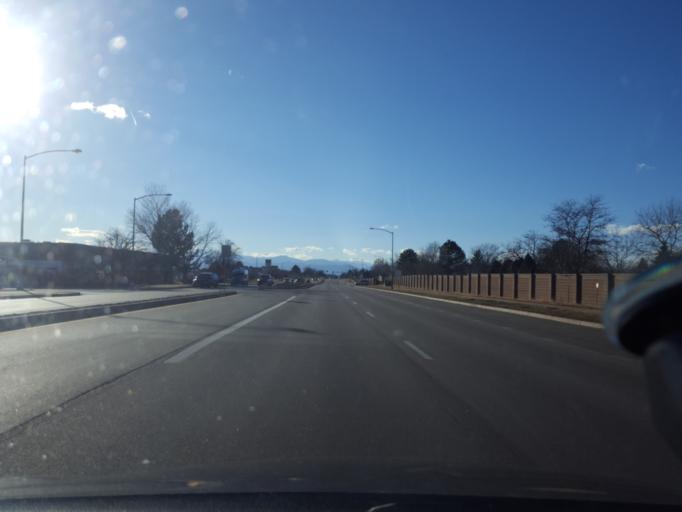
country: US
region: Colorado
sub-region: Adams County
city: Aurora
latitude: 39.7256
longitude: -104.7937
